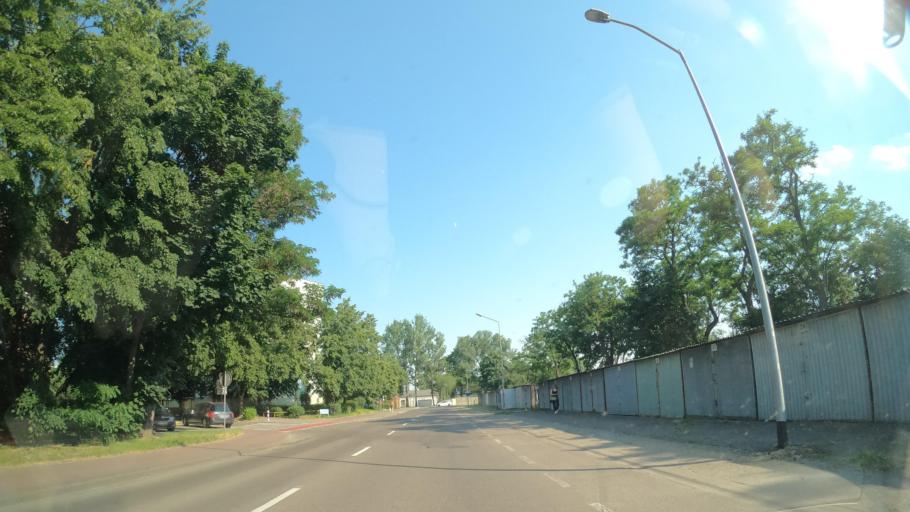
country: PL
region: West Pomeranian Voivodeship
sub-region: Powiat stargardzki
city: Stargard Szczecinski
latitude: 53.3368
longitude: 15.0062
